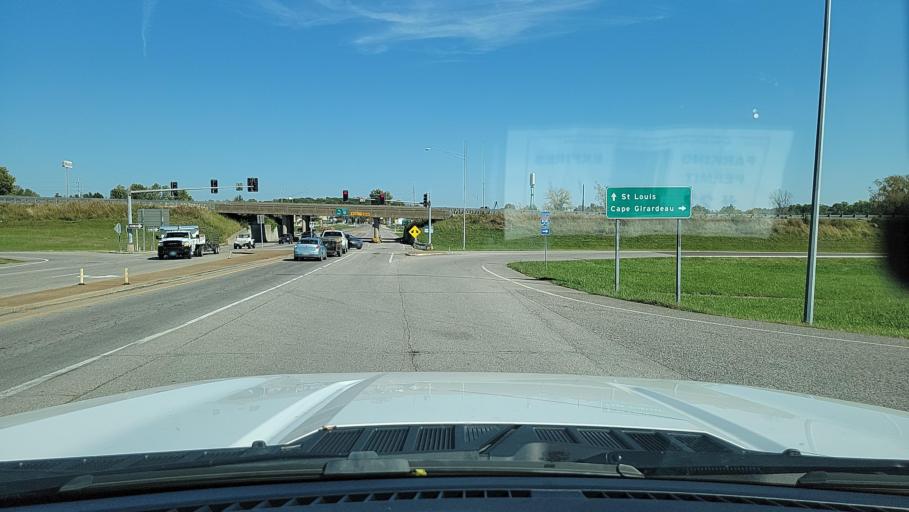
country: US
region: Missouri
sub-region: Jefferson County
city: Pevely
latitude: 38.2869
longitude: -90.4046
